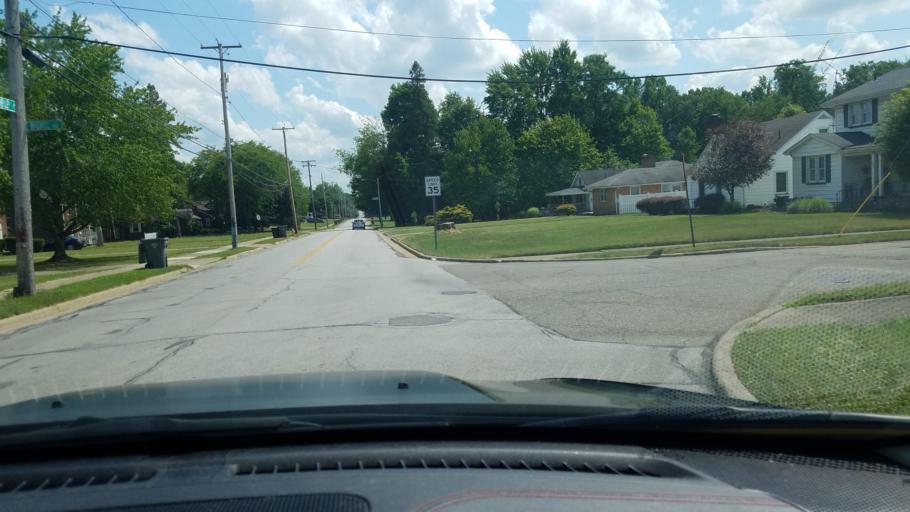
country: US
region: Ohio
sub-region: Mahoning County
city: Youngstown
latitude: 41.0935
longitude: -80.6999
